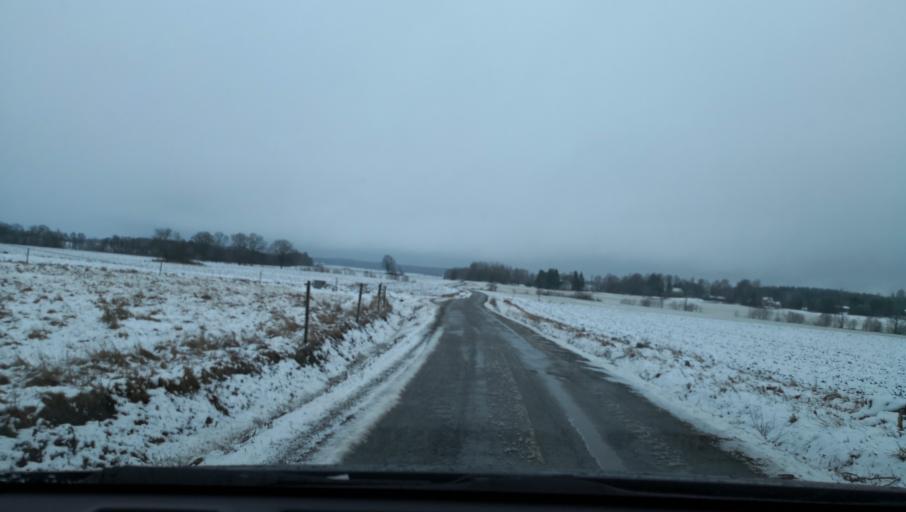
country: SE
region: Vaestmanland
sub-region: Kopings Kommun
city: Kolsva
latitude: 59.5417
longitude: 15.8816
